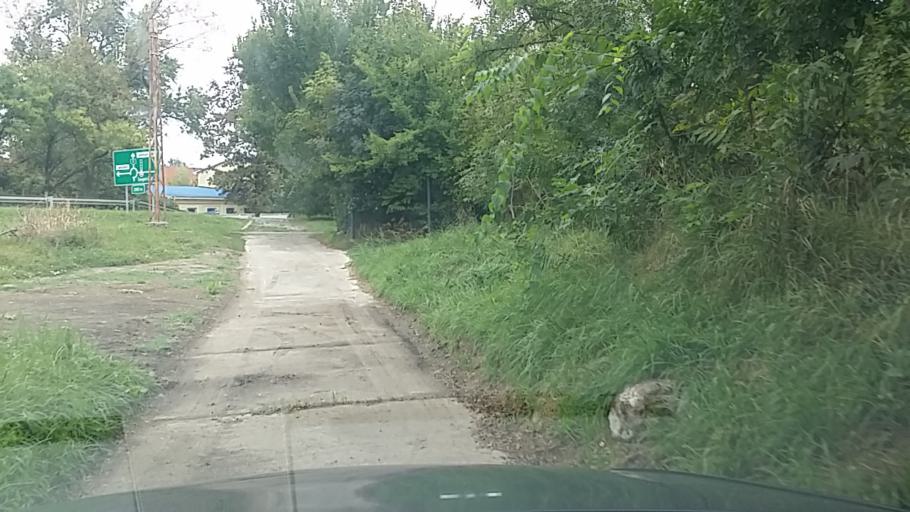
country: HU
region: Csongrad
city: Szeged
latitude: 46.2389
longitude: 20.1167
